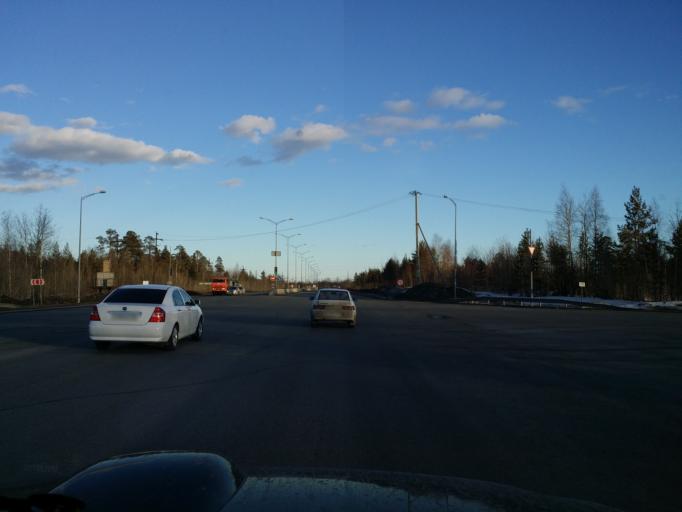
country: RU
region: Khanty-Mansiyskiy Avtonomnyy Okrug
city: Nizhnevartovsk
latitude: 60.9921
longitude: 76.4346
